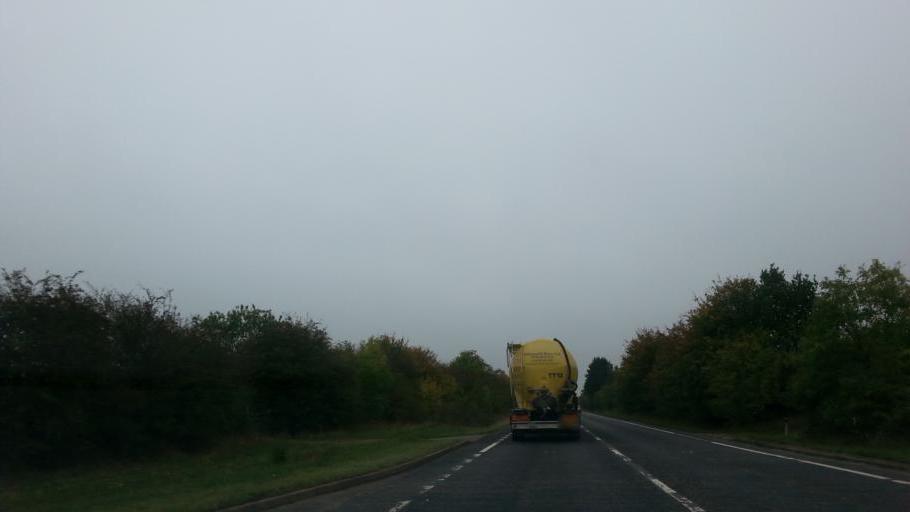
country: GB
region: England
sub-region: Northamptonshire
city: Raunds
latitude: 52.3674
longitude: -0.5282
